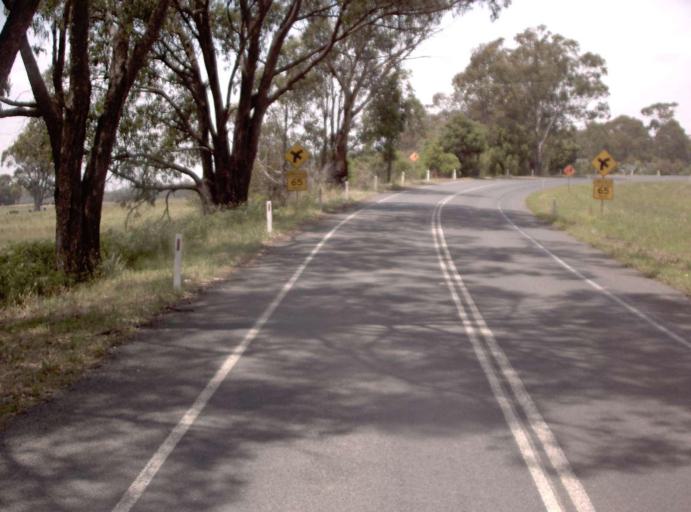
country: AU
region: Victoria
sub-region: Latrobe
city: Traralgon
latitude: -38.3801
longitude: 146.7578
